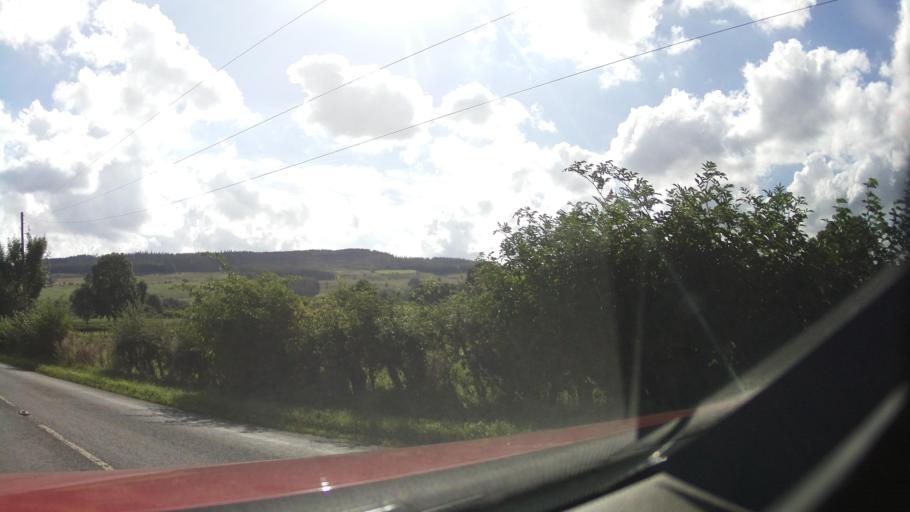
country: GB
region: England
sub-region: North Yorkshire
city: Leyburn
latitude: 54.2759
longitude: -1.7793
